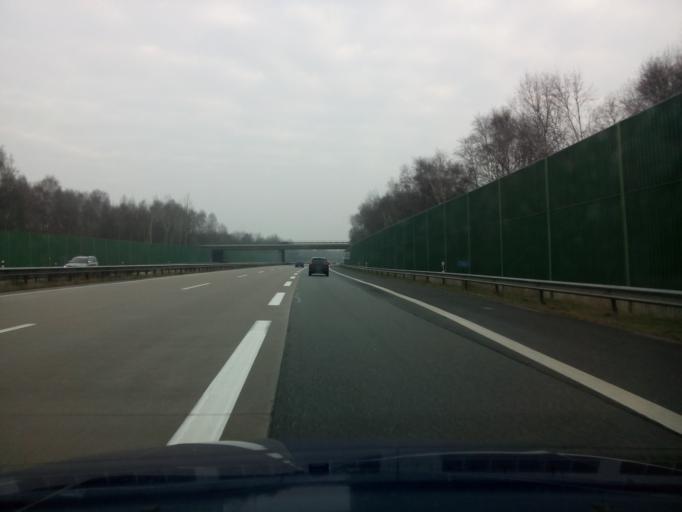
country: DE
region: Lower Saxony
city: Langen
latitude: 53.5792
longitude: 8.6216
